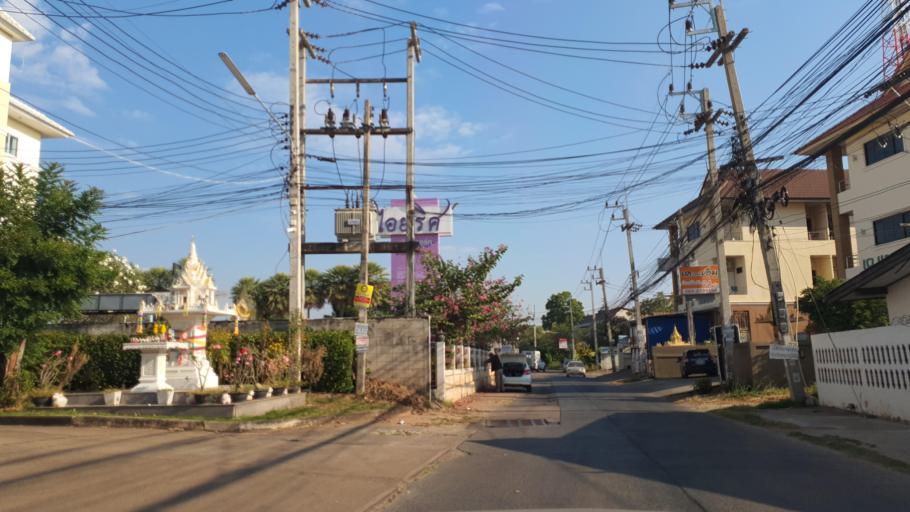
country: TH
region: Khon Kaen
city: Khon Kaen
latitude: 16.4198
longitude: 102.8055
